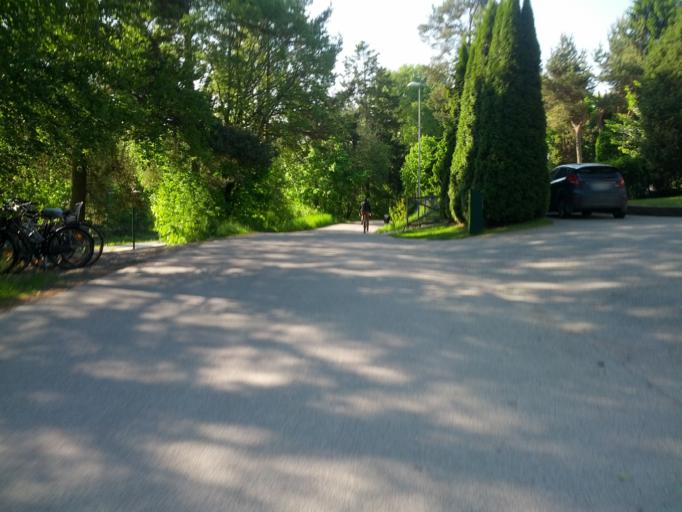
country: SE
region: Stockholm
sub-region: Taby Kommun
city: Taby
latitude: 59.4545
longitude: 18.0628
